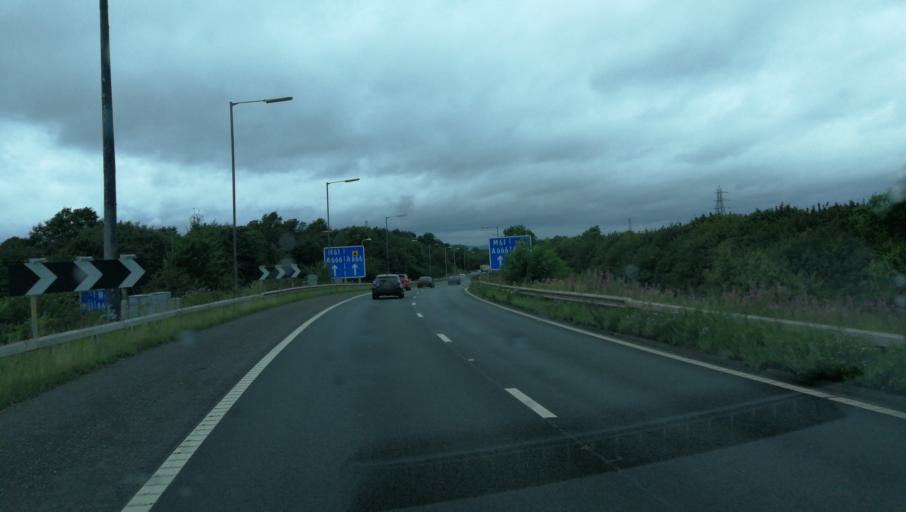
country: GB
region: England
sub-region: Borough of Bolton
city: Kearsley
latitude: 53.5246
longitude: -2.3613
